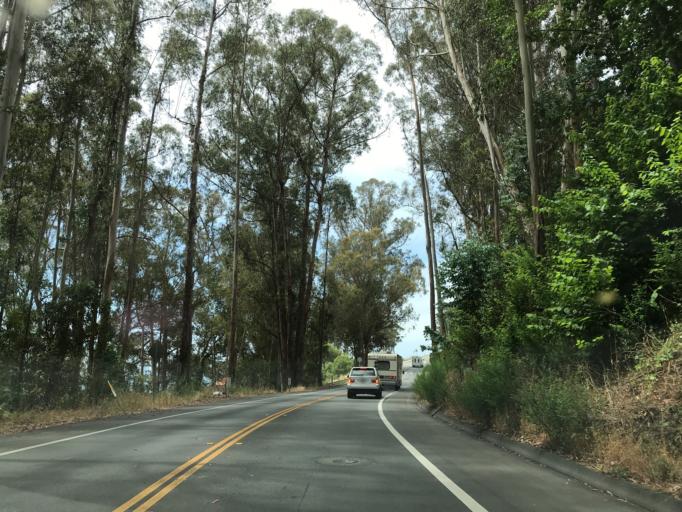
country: US
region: California
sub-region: Santa Cruz County
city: Capitola
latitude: 36.9803
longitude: -121.9385
